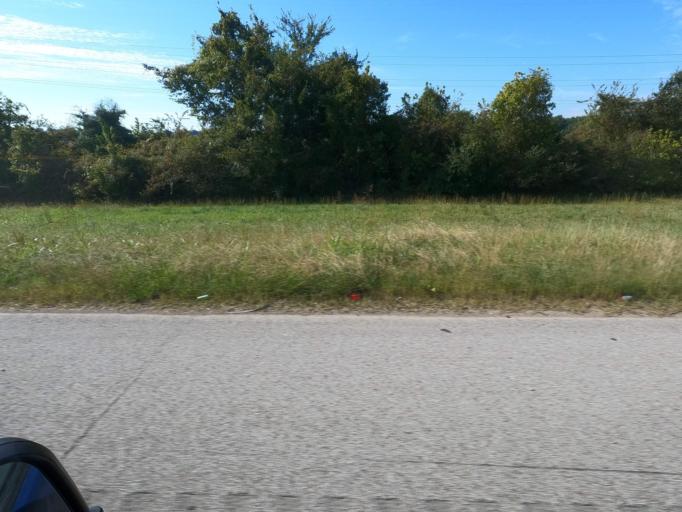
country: US
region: Tennessee
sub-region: Shelby County
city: Millington
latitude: 35.3270
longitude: -89.8871
